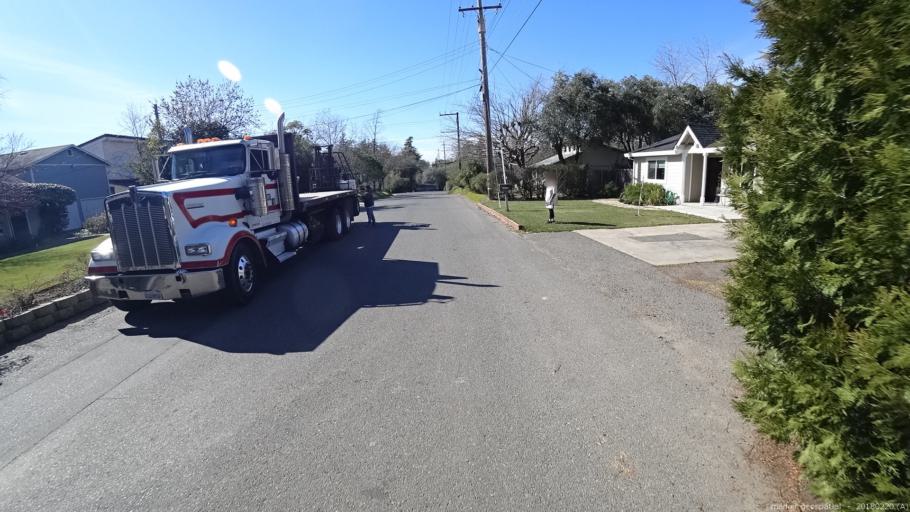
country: US
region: California
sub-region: Sacramento County
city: Orangevale
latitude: 38.6926
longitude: -121.2010
